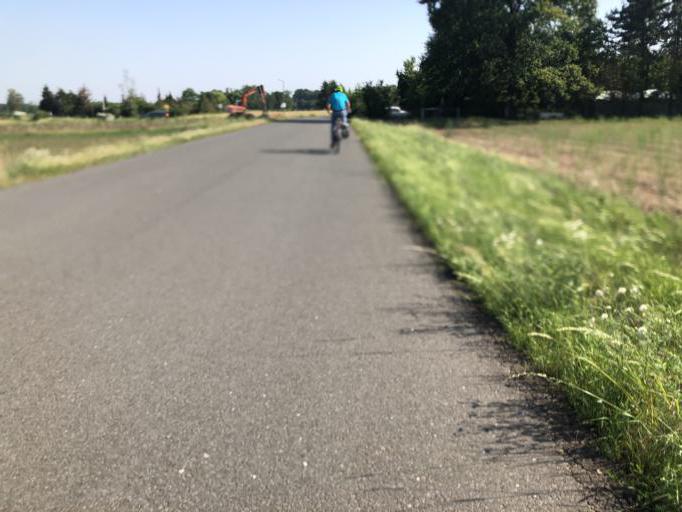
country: DE
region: Bavaria
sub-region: Regierungsbezirk Mittelfranken
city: Erlangen
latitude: 49.5354
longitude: 11.0280
